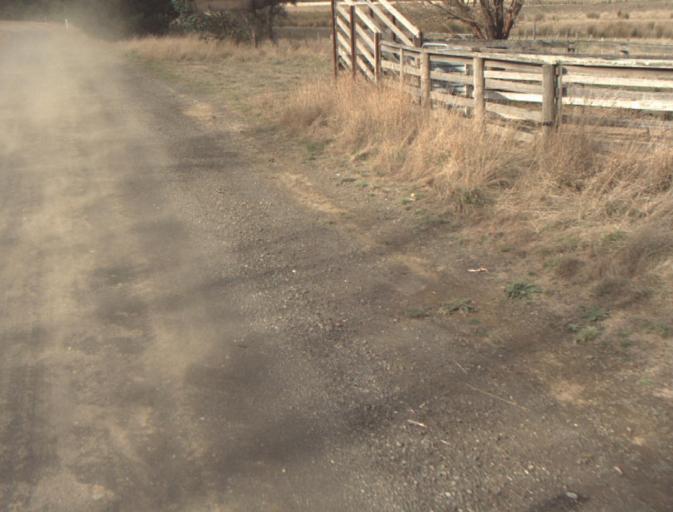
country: AU
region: Tasmania
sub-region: Launceston
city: Mayfield
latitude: -41.2113
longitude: 147.1825
